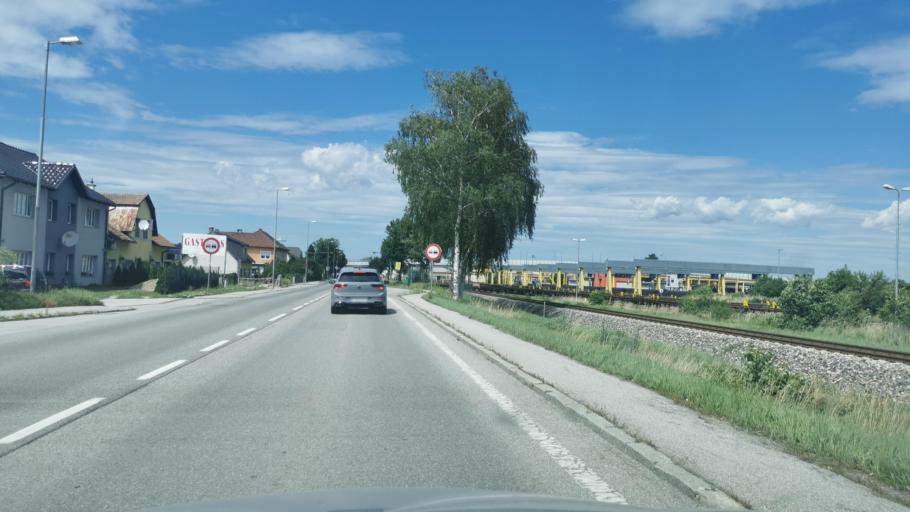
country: AT
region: Lower Austria
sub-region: Politischer Bezirk Sankt Polten
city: Wilhelmsburg
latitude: 48.1494
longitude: 15.6142
